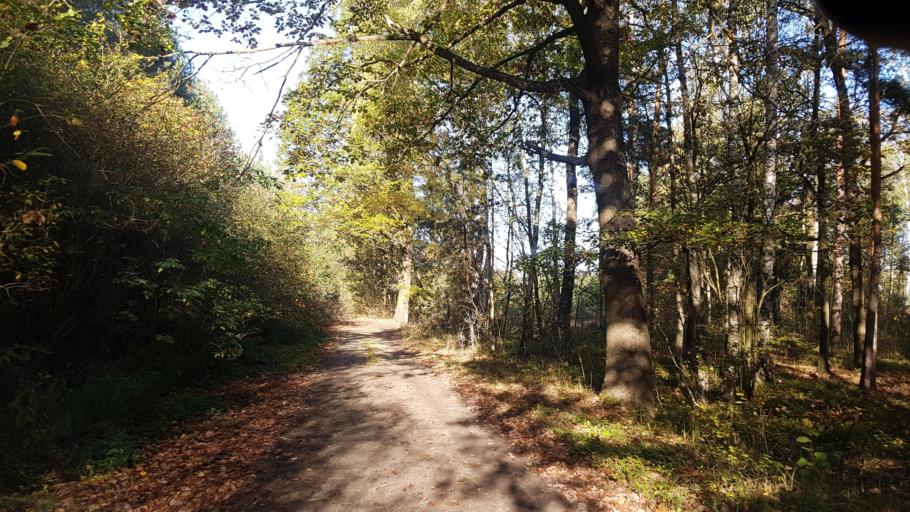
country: DE
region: Brandenburg
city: Ruckersdorf
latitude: 51.5501
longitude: 13.5369
